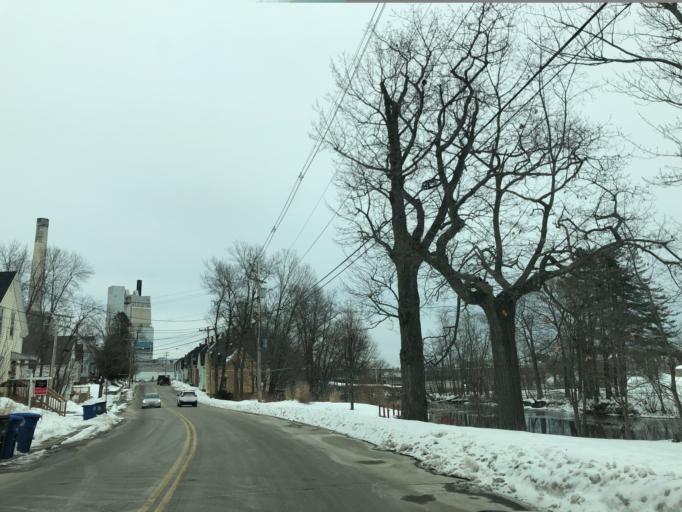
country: US
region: Maine
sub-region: Cumberland County
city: Westbrook
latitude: 43.6821
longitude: -70.3559
